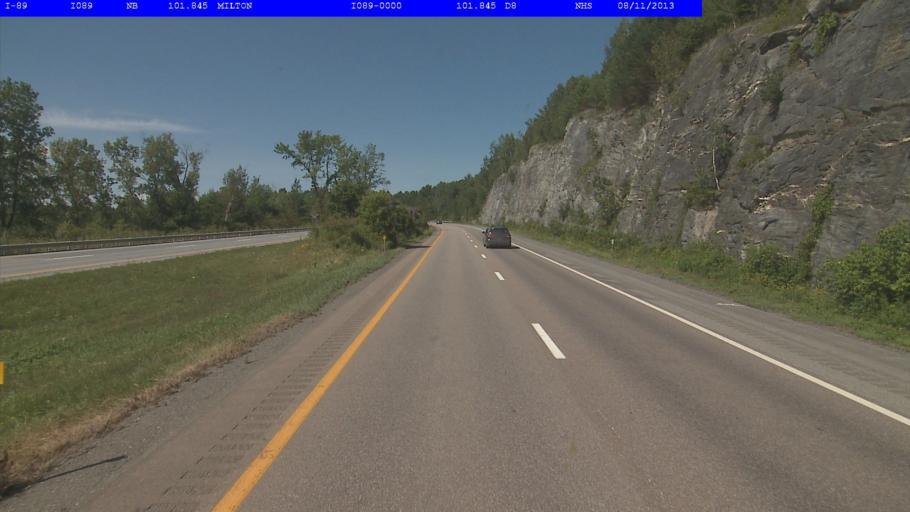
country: US
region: Vermont
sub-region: Chittenden County
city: Milton
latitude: 44.6400
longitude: -73.1398
